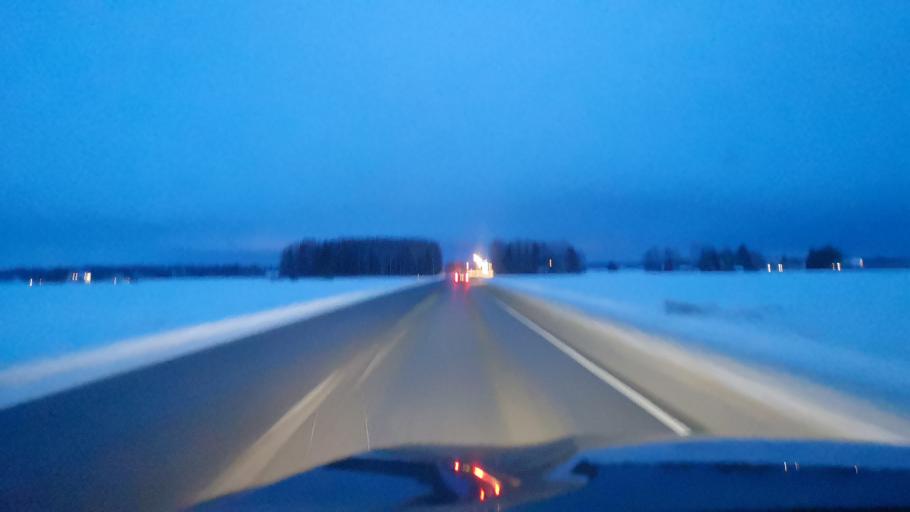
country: FI
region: Varsinais-Suomi
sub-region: Loimaa
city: Loimaa
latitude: 60.8809
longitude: 23.0797
